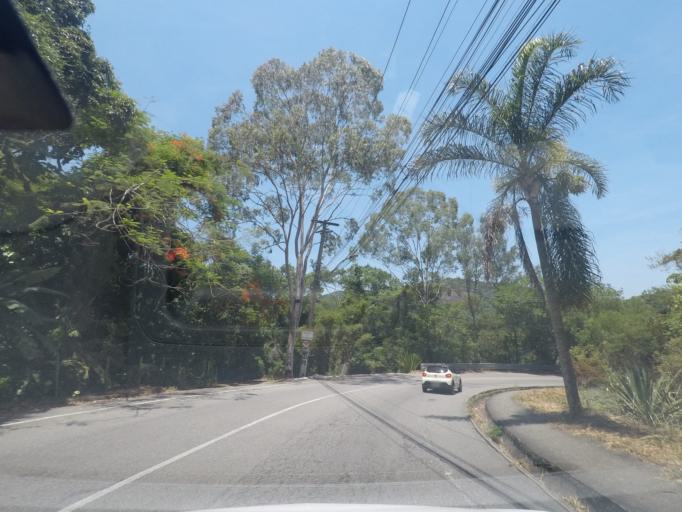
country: BR
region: Rio de Janeiro
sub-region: Niteroi
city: Niteroi
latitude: -22.9239
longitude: -43.0656
